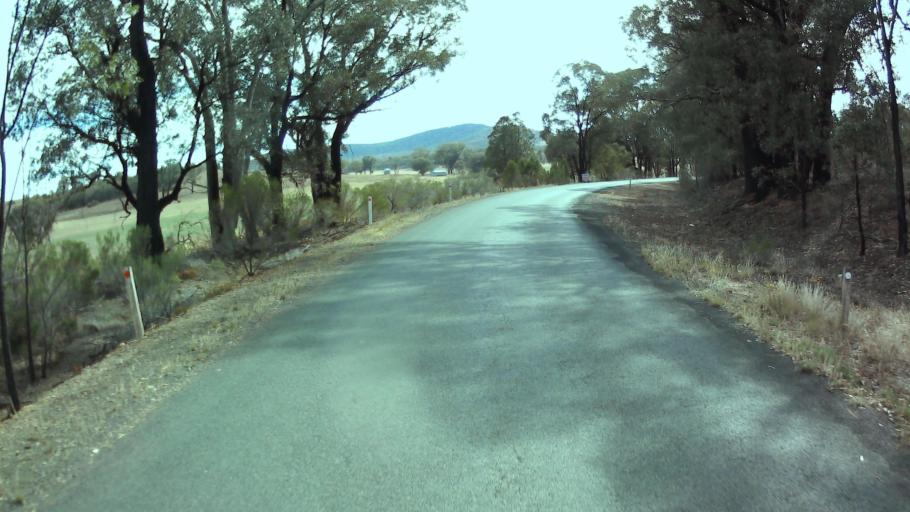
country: AU
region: New South Wales
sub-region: Weddin
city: Grenfell
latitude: -33.8434
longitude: 148.2369
